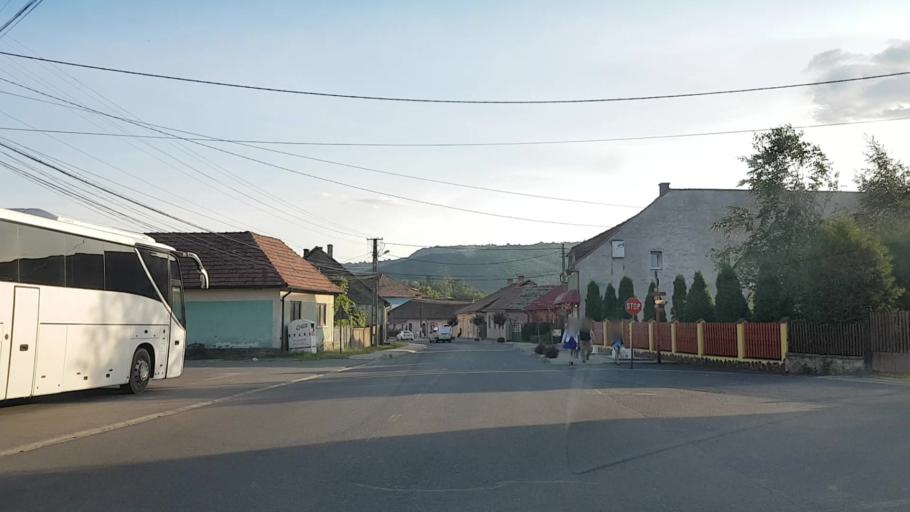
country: RO
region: Harghita
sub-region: Comuna Praid
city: Praid
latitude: 46.5538
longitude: 25.1280
